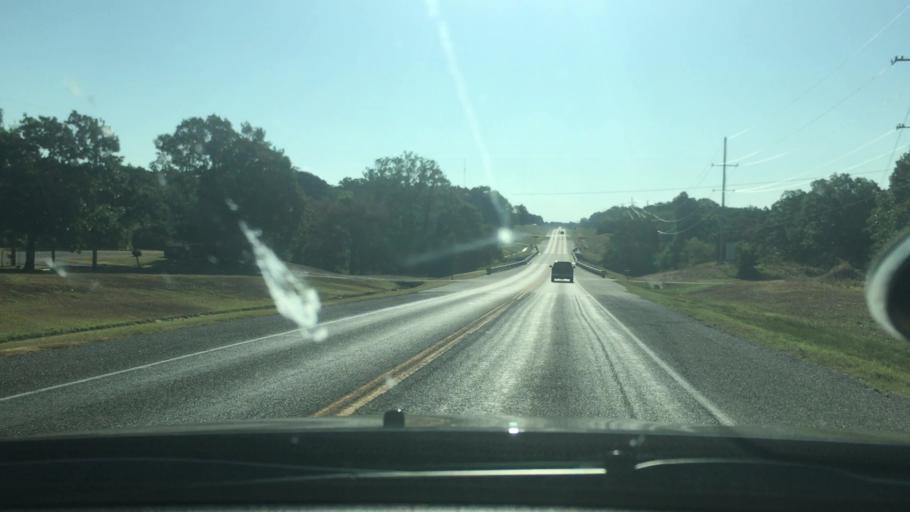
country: US
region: Oklahoma
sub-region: Johnston County
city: Tishomingo
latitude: 34.2368
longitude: -96.7196
